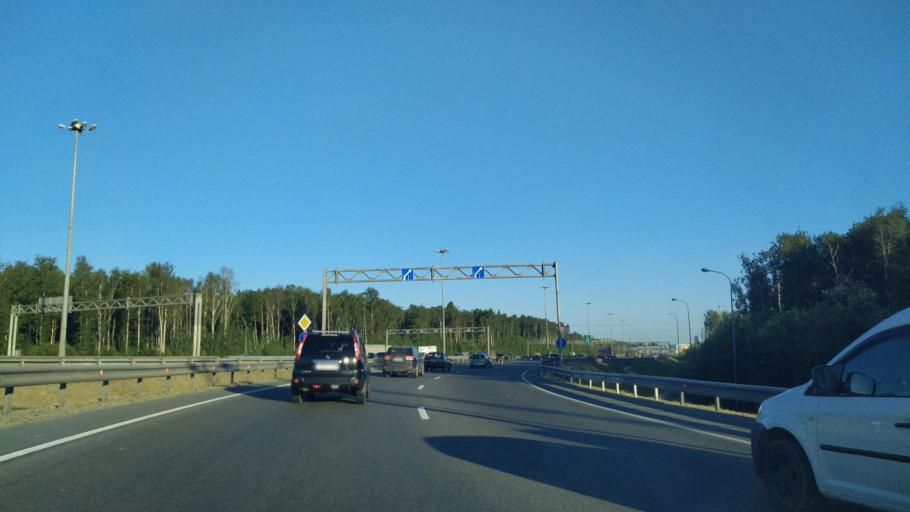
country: RU
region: Leningrad
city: Rybatskoye
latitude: 59.8887
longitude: 30.5234
